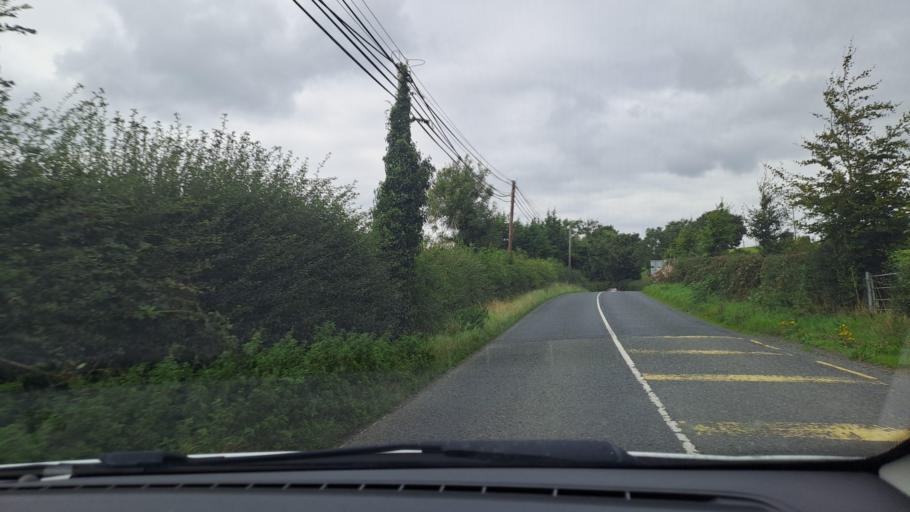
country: IE
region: Ulster
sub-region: An Cabhan
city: Bailieborough
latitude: 54.0023
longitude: -6.9072
